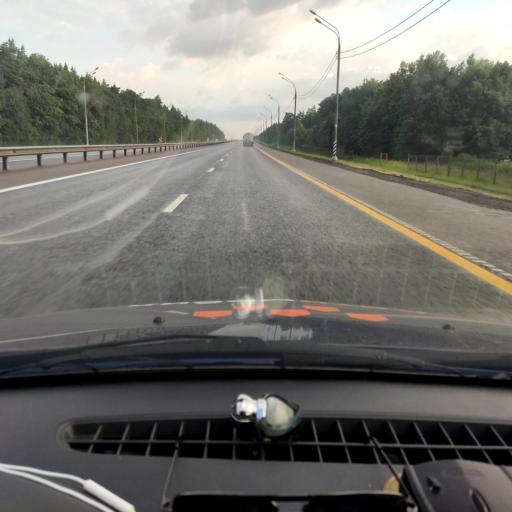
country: RU
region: Lipetsk
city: Zadonsk
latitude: 52.3472
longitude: 38.9522
